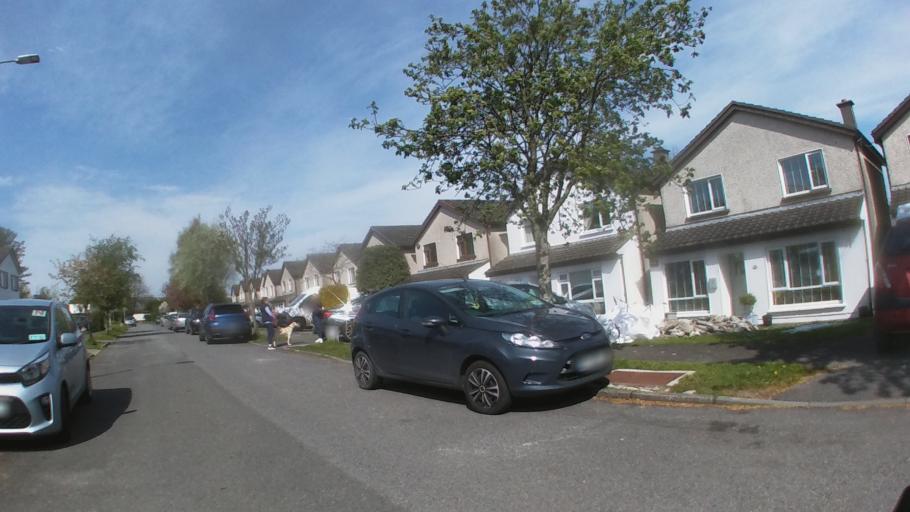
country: IE
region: Leinster
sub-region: Kilkenny
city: Kilkenny
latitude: 52.6641
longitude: -7.2592
